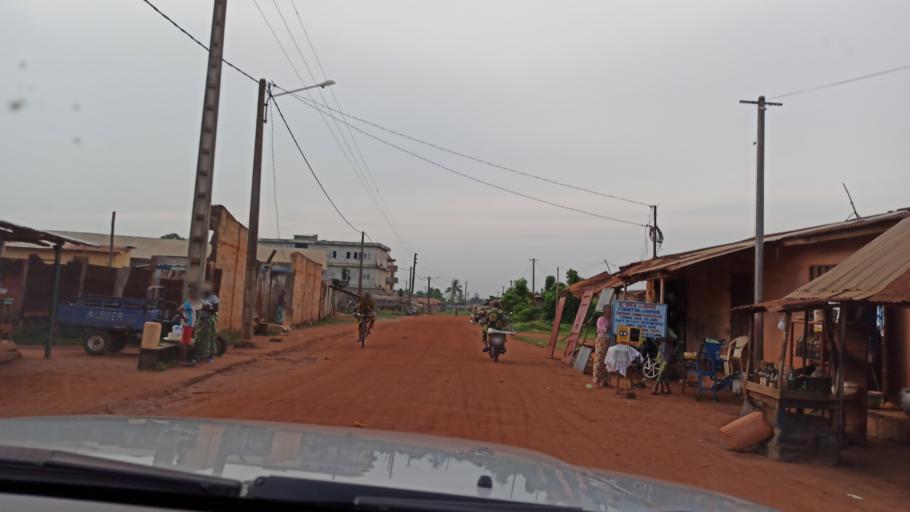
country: BJ
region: Queme
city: Porto-Novo
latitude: 6.5220
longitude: 2.6734
